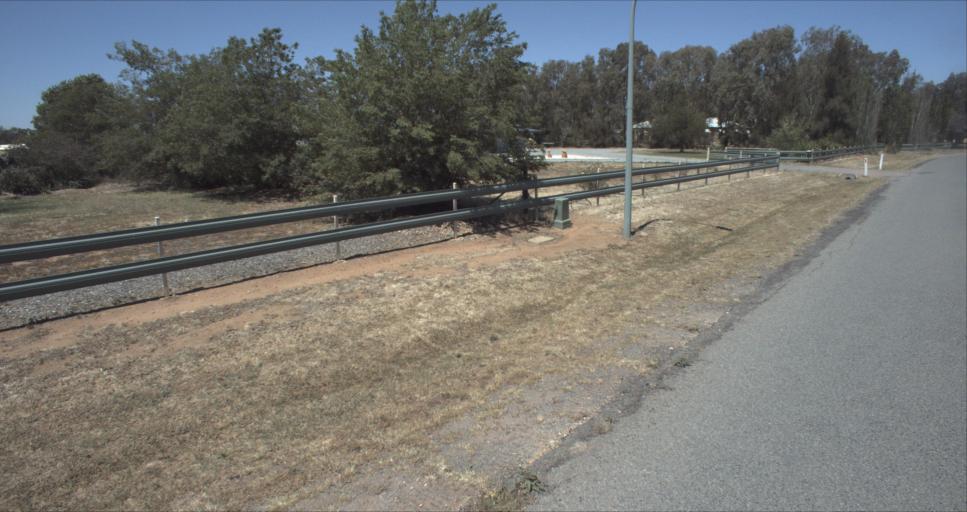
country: AU
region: New South Wales
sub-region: Leeton
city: Leeton
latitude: -34.5288
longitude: 146.3986
